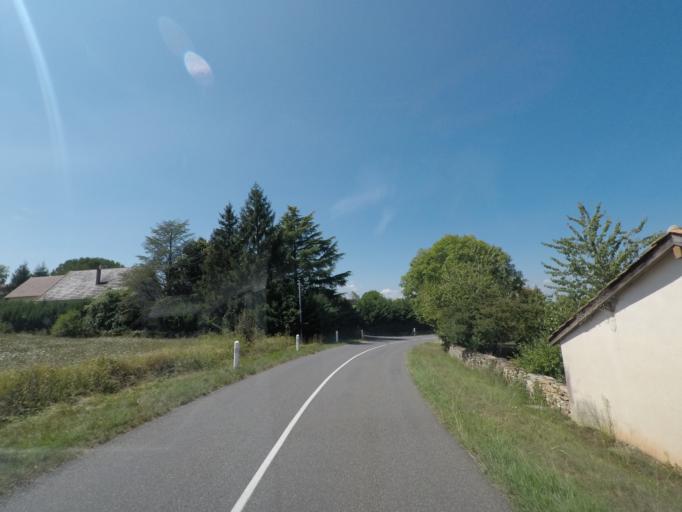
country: FR
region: Midi-Pyrenees
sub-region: Departement de l'Aveyron
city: Capdenac-Gare
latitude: 44.6057
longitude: 2.0710
